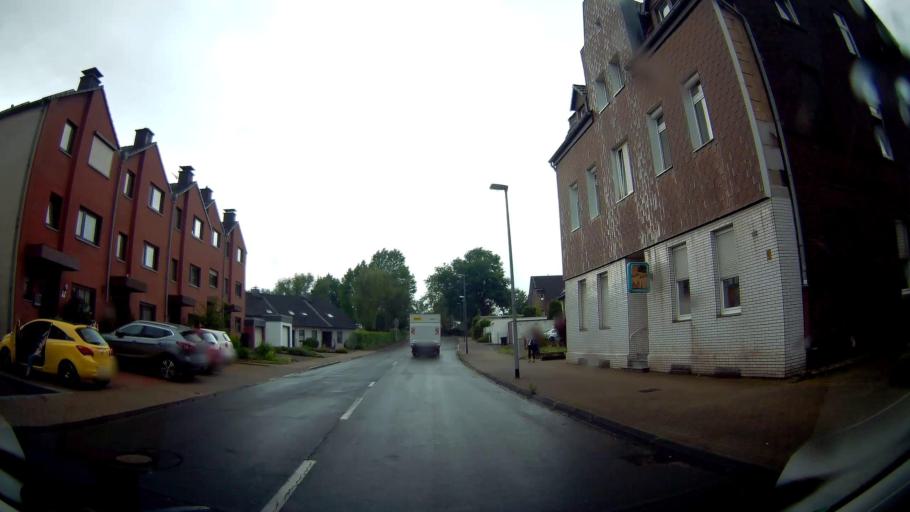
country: DE
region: North Rhine-Westphalia
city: Bochum-Hordel
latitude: 51.5066
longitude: 7.1654
